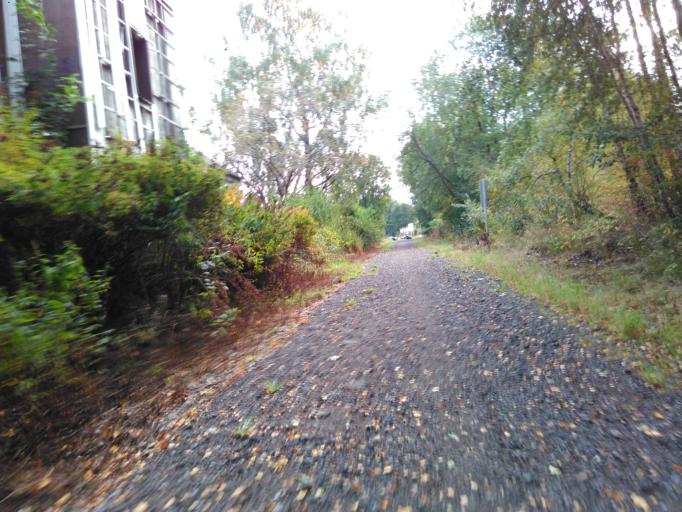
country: BE
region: Wallonia
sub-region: Province du Luxembourg
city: Neufchateau
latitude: 49.9072
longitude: 5.4574
